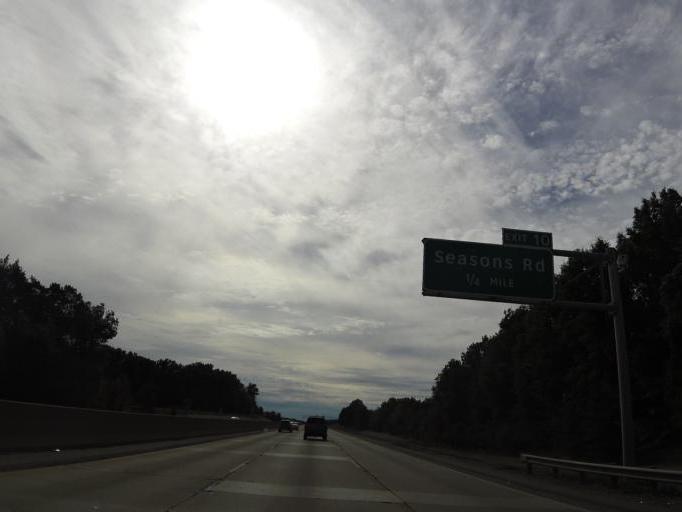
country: US
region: Ohio
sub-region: Summit County
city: Hudson
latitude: 41.2108
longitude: -81.4869
